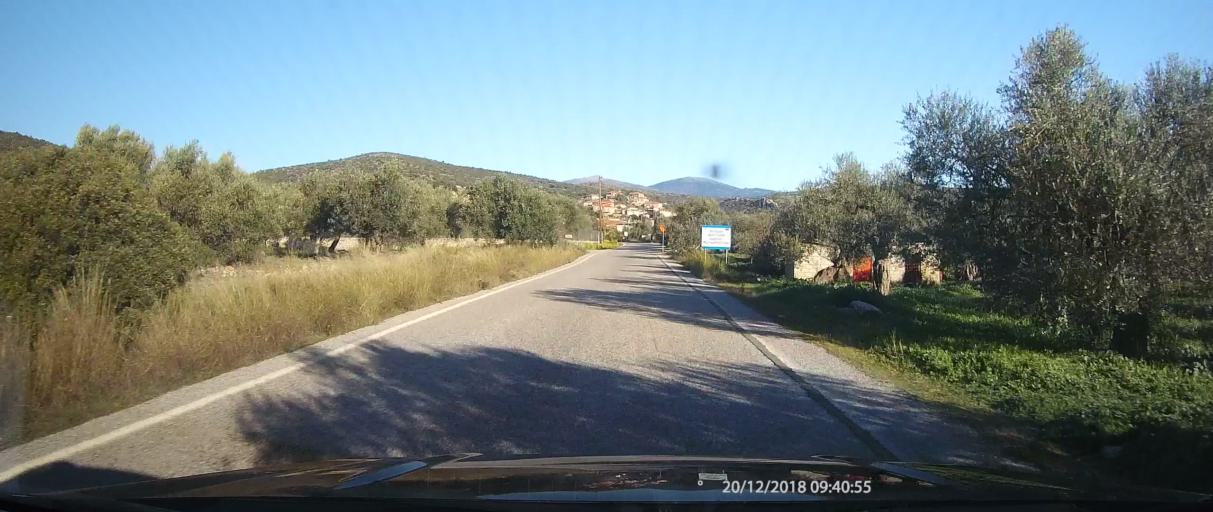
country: GR
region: Peloponnese
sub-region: Nomos Lakonias
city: Yerakion
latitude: 36.9491
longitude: 22.7663
